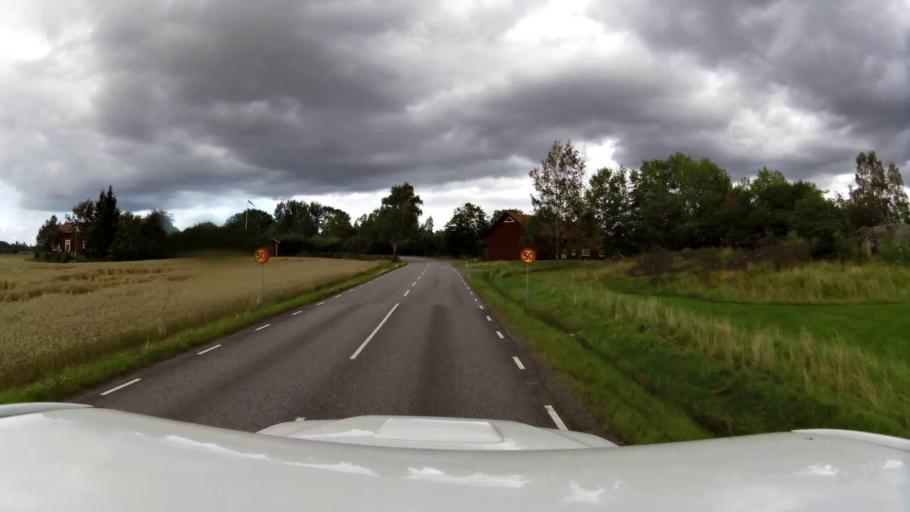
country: SE
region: OEstergoetland
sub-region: Linkopings Kommun
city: Linghem
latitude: 58.4287
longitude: 15.7771
